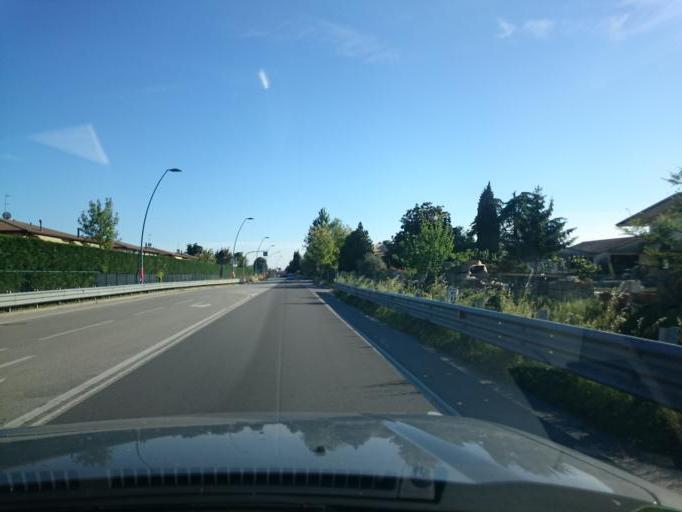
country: IT
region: Veneto
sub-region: Provincia di Venezia
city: Santa Maria di Sala
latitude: 45.5114
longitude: 12.0324
